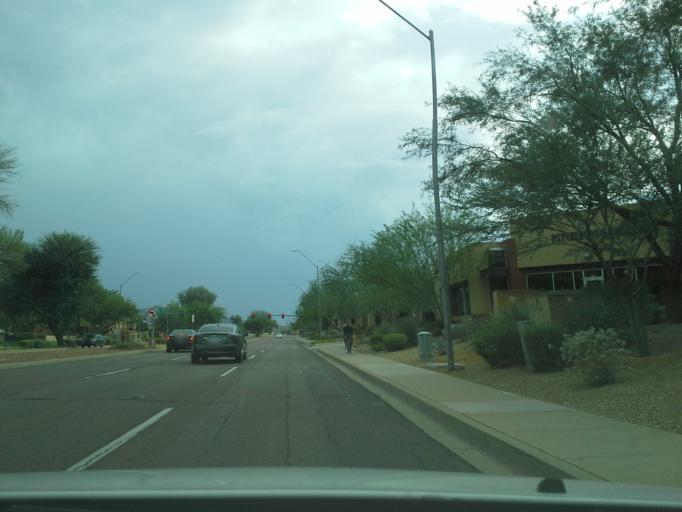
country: US
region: Arizona
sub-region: Maricopa County
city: Paradise Valley
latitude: 33.5879
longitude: -111.9780
